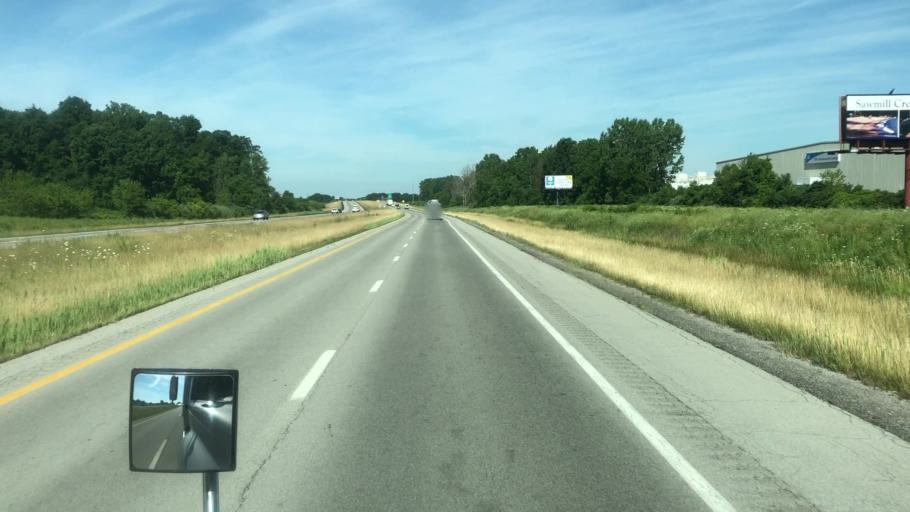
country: US
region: Ohio
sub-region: Erie County
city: Huron
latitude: 41.3694
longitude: -82.5338
